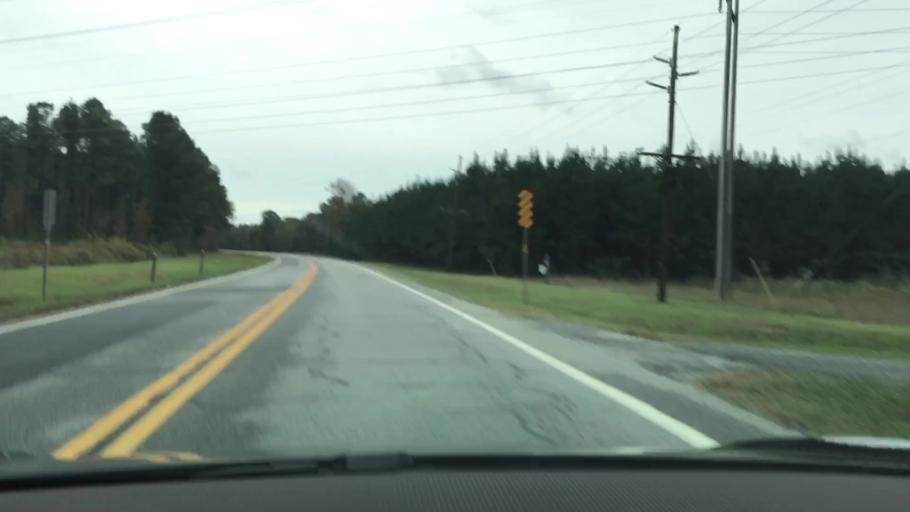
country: US
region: Georgia
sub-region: Warren County
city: Warrenton
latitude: 33.3910
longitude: -82.6463
